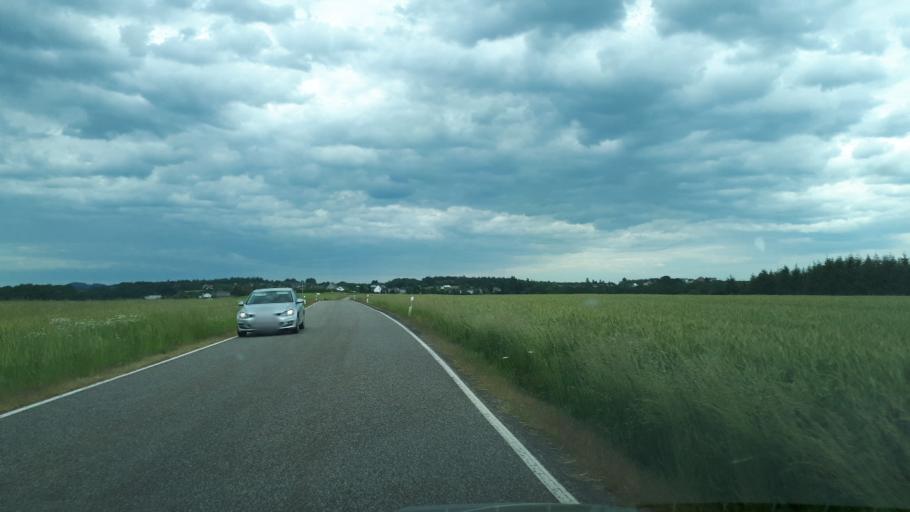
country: DE
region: Rheinland-Pfalz
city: Auderath
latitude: 50.1798
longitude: 6.9922
